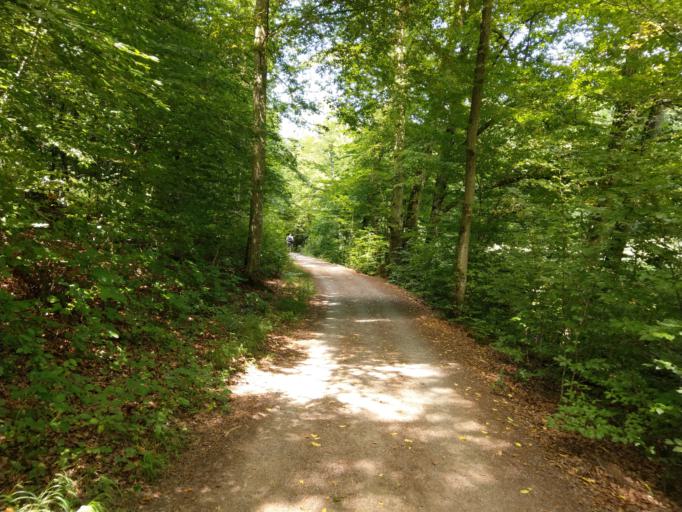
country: DE
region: Baden-Wuerttemberg
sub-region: Regierungsbezirk Stuttgart
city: Gerlingen
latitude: 48.7643
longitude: 9.0859
